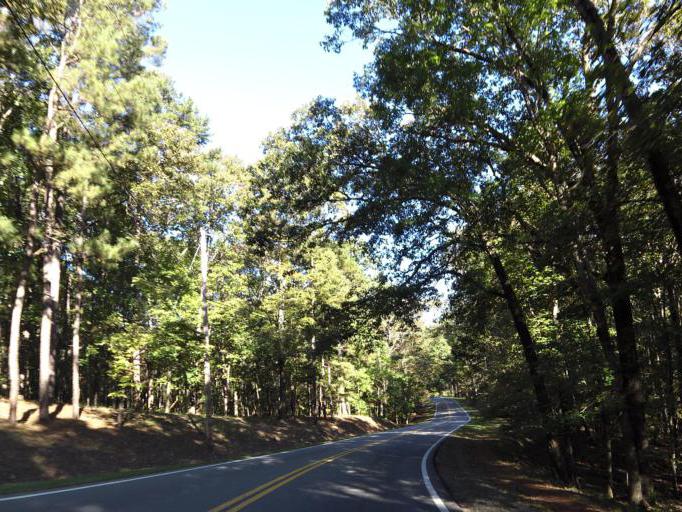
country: US
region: Georgia
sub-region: Bartow County
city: Emerson
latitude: 34.1478
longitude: -84.7110
